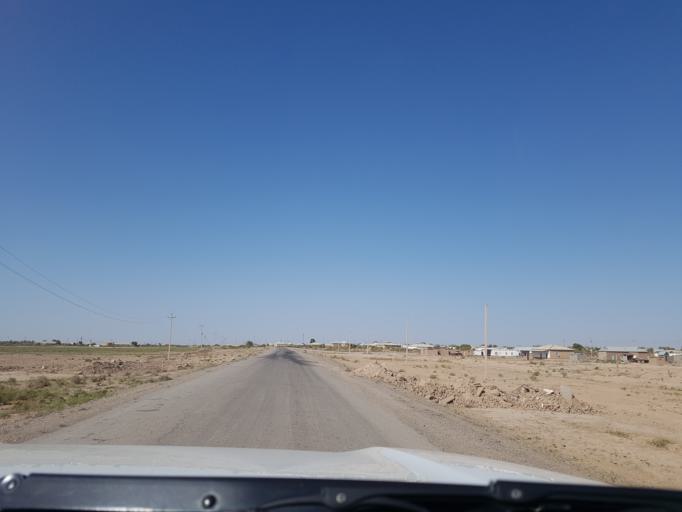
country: IR
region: Razavi Khorasan
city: Sarakhs
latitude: 36.5100
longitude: 61.2533
